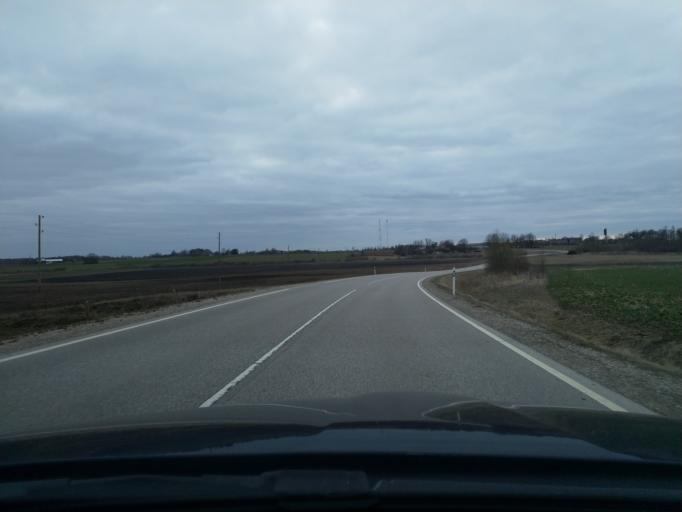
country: LV
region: Talsu Rajons
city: Sabile
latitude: 56.9430
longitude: 22.4180
